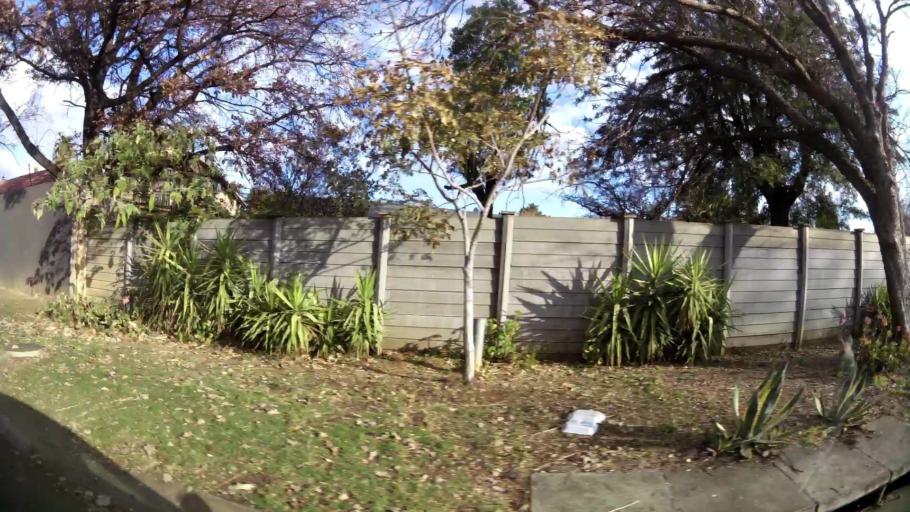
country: ZA
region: Orange Free State
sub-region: Mangaung Metropolitan Municipality
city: Bloemfontein
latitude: -29.1015
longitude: 26.2029
